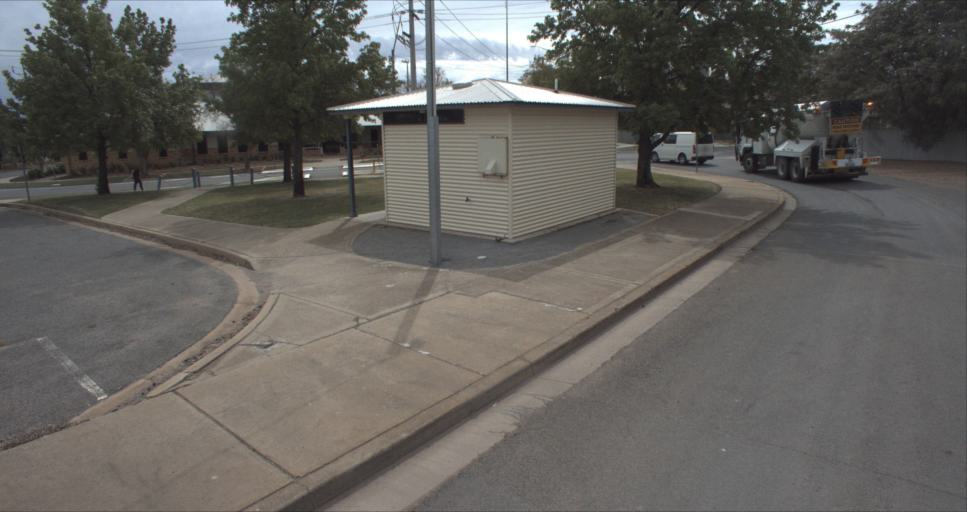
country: AU
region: New South Wales
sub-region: Leeton
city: Leeton
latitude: -34.5509
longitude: 146.4051
